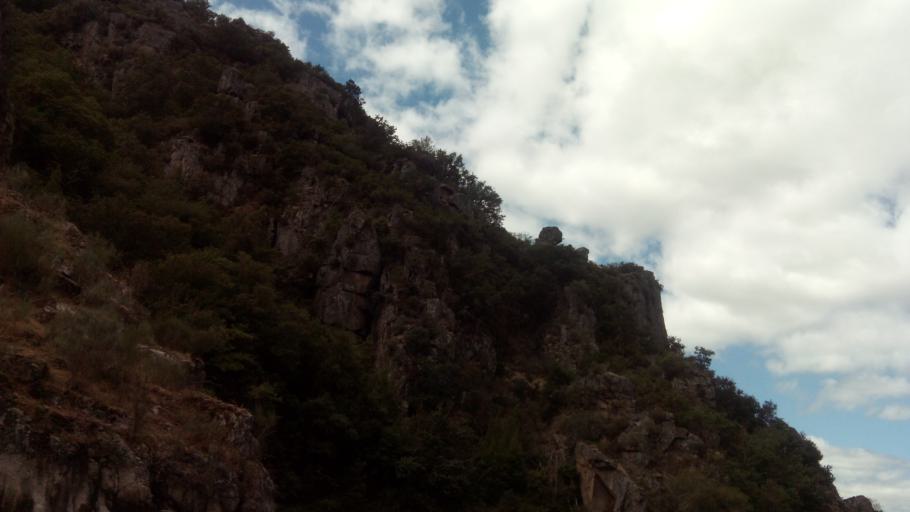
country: ES
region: Galicia
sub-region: Provincia de Lugo
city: Sober
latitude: 42.4051
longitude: -7.6311
